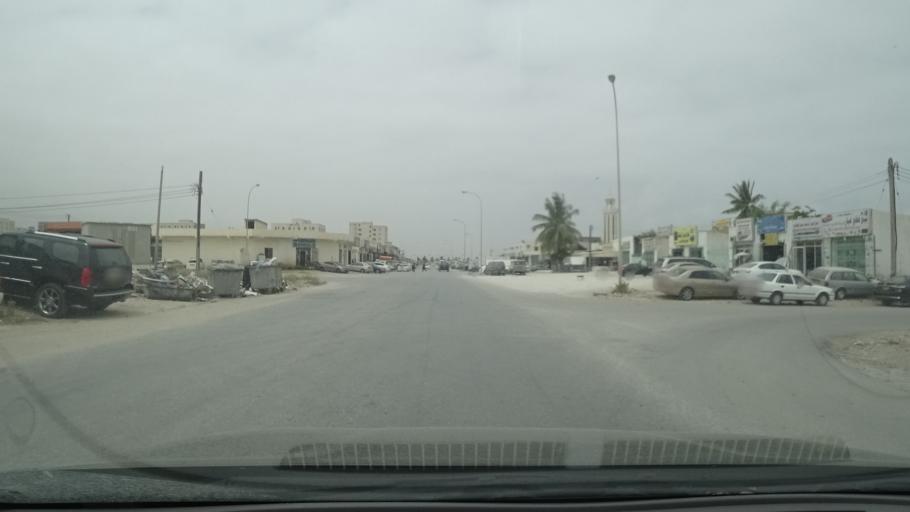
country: OM
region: Zufar
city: Salalah
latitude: 17.0242
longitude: 54.0520
